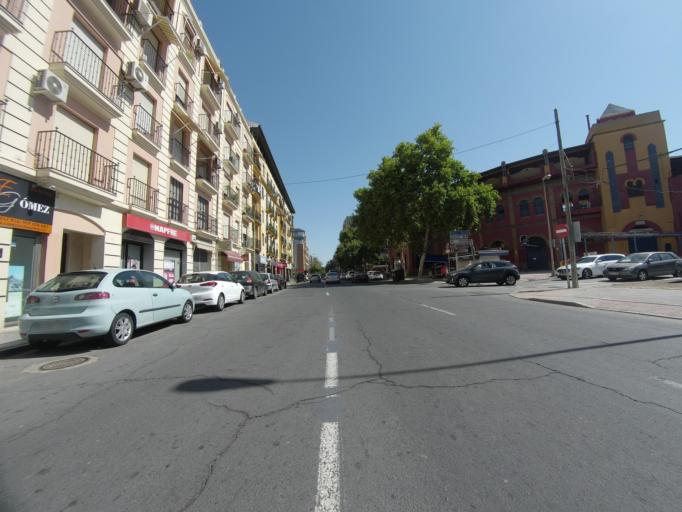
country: ES
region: Andalusia
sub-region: Provincia de Huelva
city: Huelva
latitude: 37.2650
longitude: -6.9525
